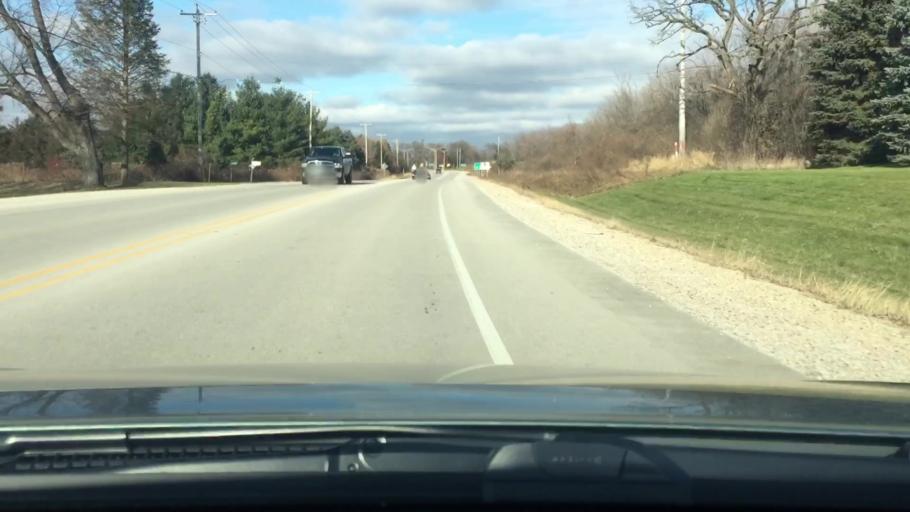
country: US
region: Wisconsin
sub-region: Waukesha County
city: Wales
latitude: 42.9843
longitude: -88.3797
